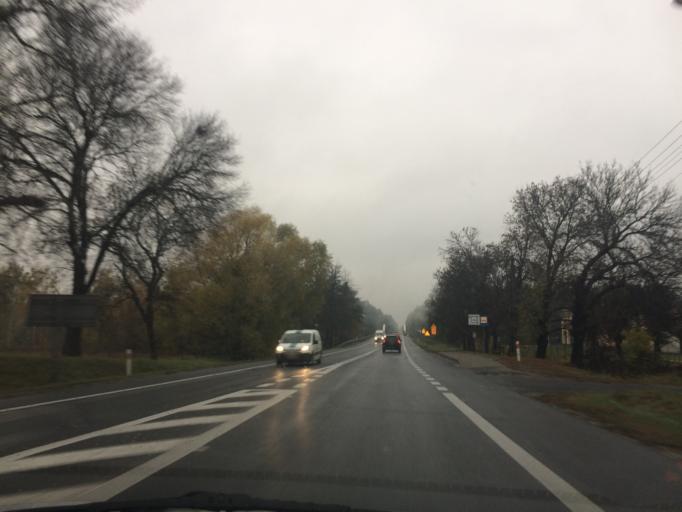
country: PL
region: Masovian Voivodeship
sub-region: Powiat otwocki
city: Otwock
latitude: 52.1377
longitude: 21.3343
